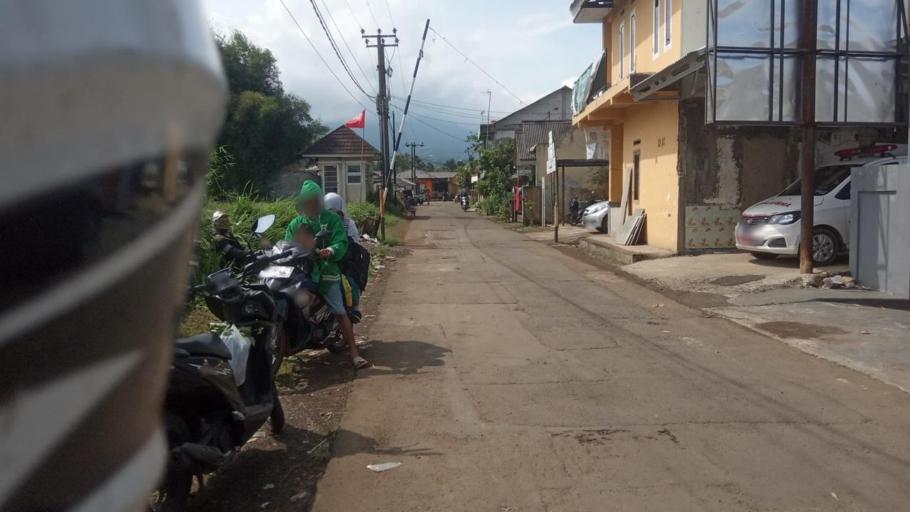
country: ID
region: West Java
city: Caringin
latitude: -6.6738
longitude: 106.8969
